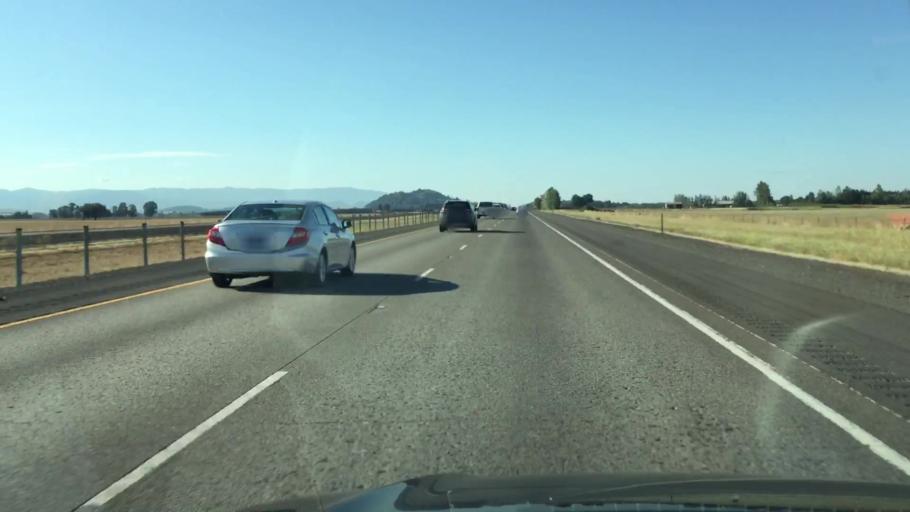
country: US
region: Oregon
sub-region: Linn County
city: Tangent
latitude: 44.5020
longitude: -123.0619
